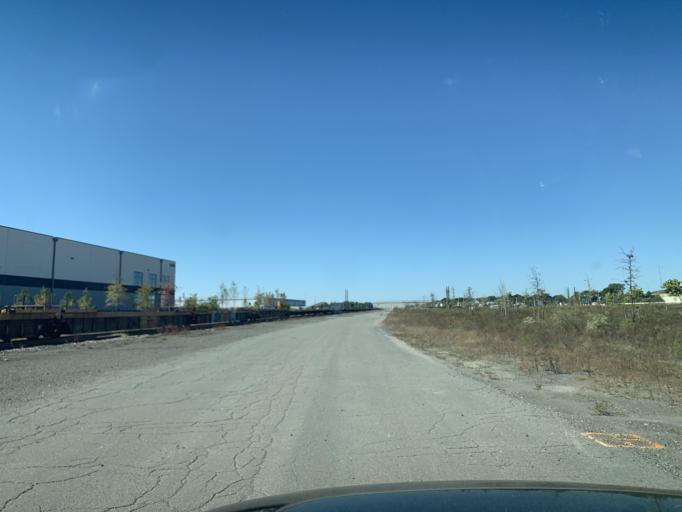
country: US
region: Maryland
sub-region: Baltimore County
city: Edgemere
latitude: 39.2355
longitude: -76.4670
